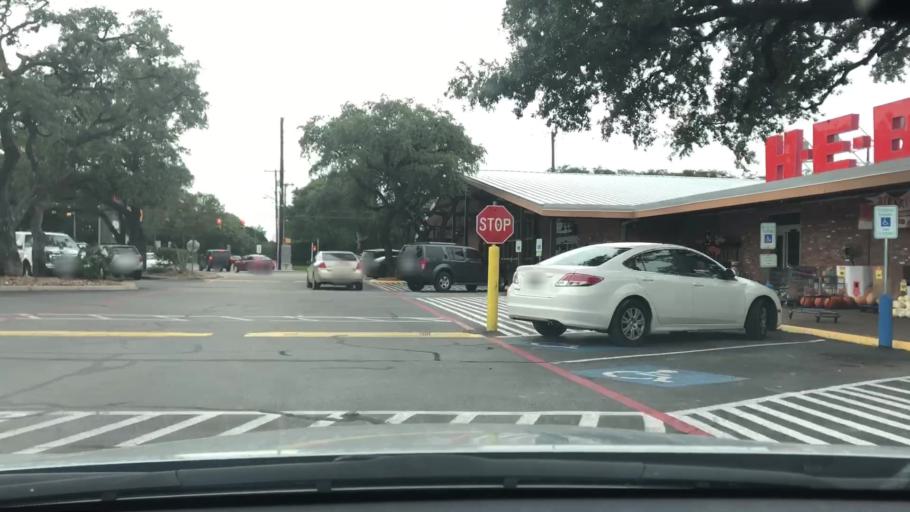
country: US
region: Texas
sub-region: Bexar County
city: Alamo Heights
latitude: 29.5074
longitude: -98.4582
